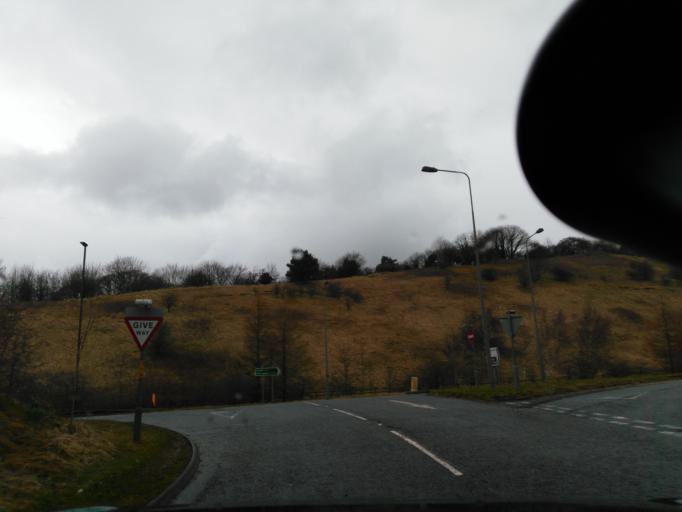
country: GB
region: England
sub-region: North Yorkshire
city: Embsay
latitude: 53.9683
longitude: -1.9973
